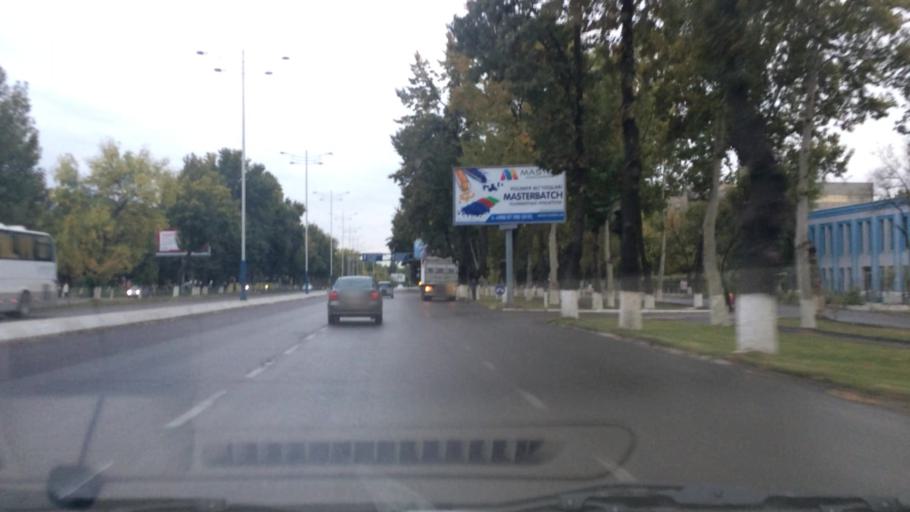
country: UZ
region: Toshkent Shahri
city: Tashkent
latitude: 41.2614
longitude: 69.1971
